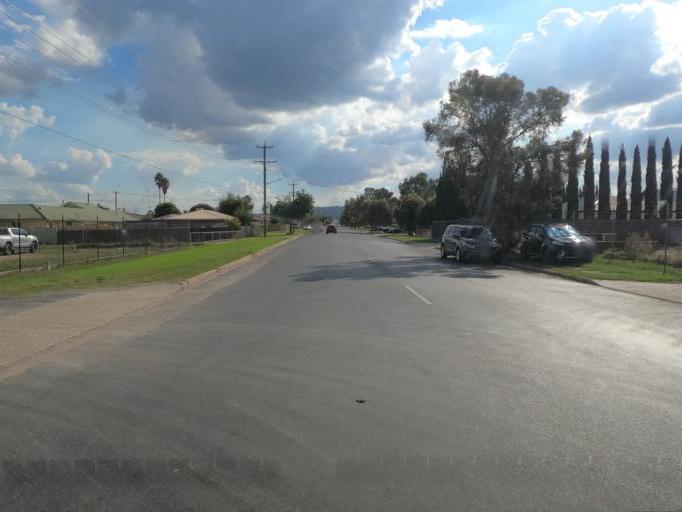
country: AU
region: New South Wales
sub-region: Albury Municipality
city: East Albury
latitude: -36.0702
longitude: 146.9412
